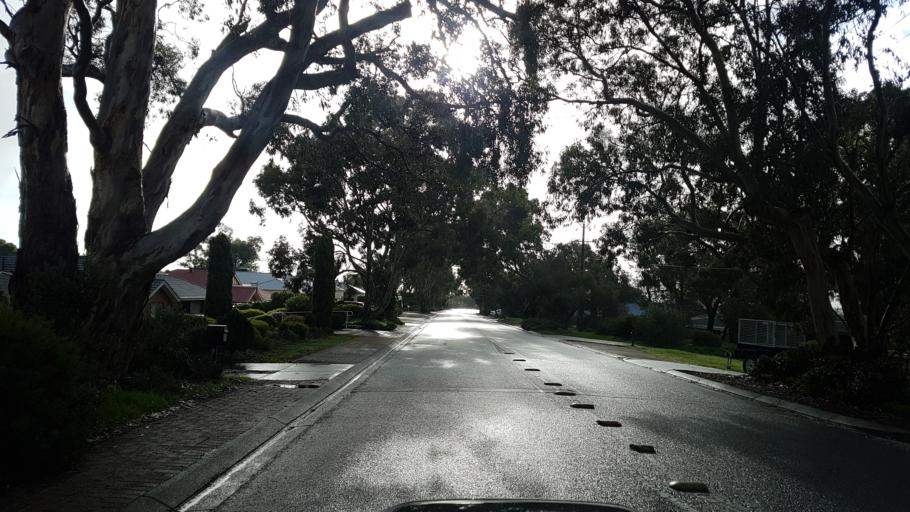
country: AU
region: South Australia
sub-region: Onkaparinga
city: Craigburn Farm
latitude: -35.0662
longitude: 138.6108
